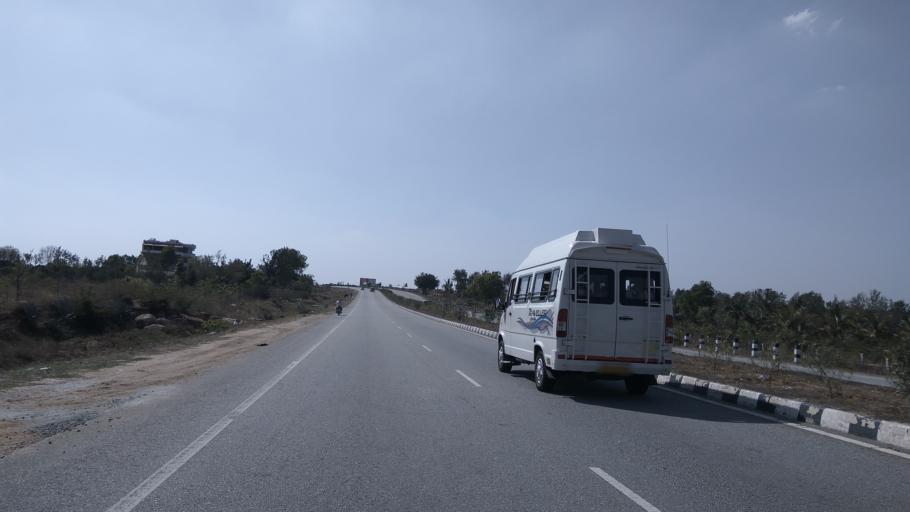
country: IN
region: Karnataka
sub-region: Kolar
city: Mulbagal
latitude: 13.1530
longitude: 78.3121
